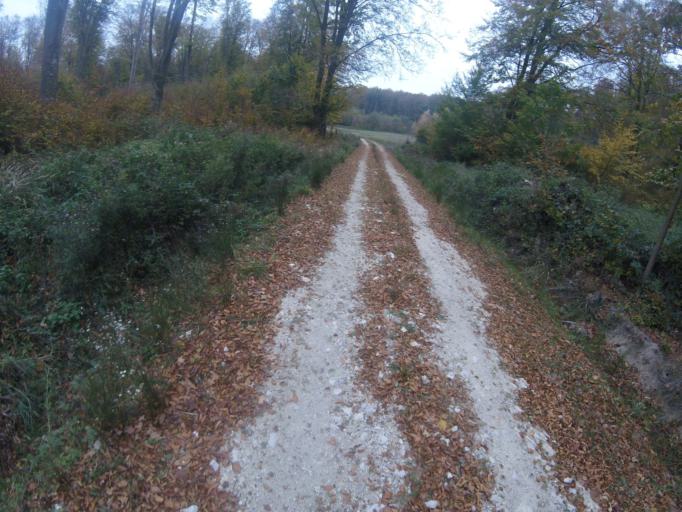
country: HU
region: Veszprem
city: Zirc
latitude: 47.2790
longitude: 17.7611
